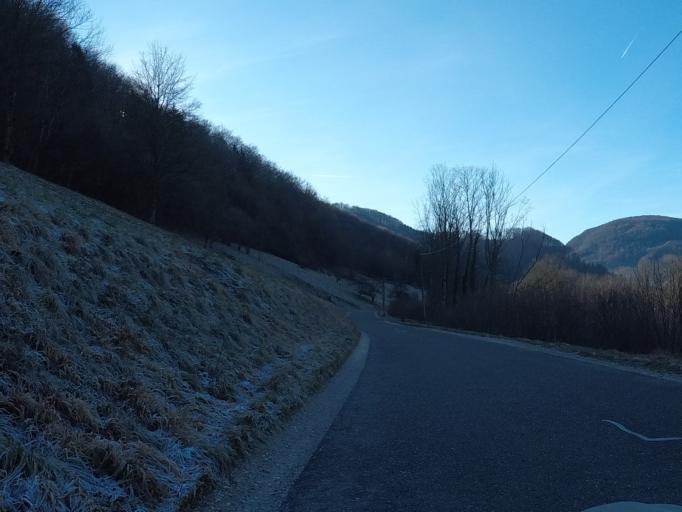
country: DE
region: Baden-Wuerttemberg
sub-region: Tuebingen Region
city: Eningen unter Achalm
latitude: 48.4452
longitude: 9.2771
